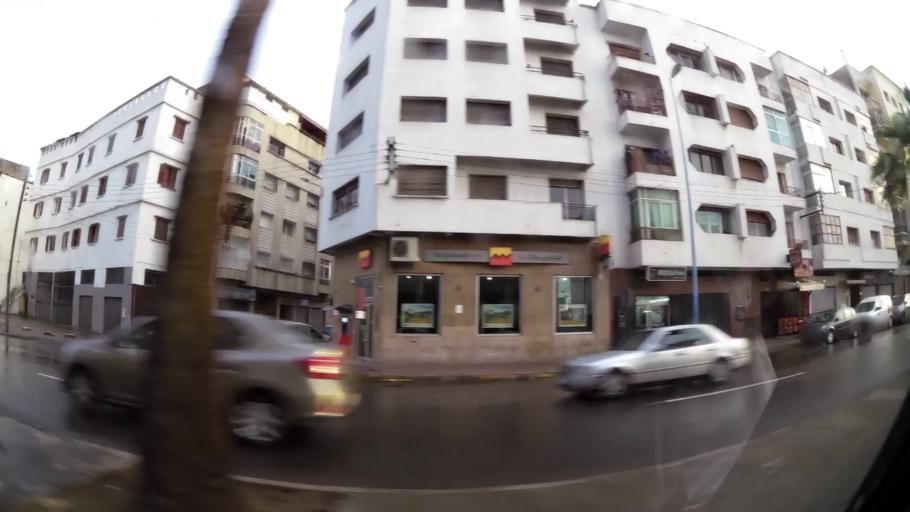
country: MA
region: Grand Casablanca
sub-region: Casablanca
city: Casablanca
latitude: 33.5863
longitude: -7.5854
